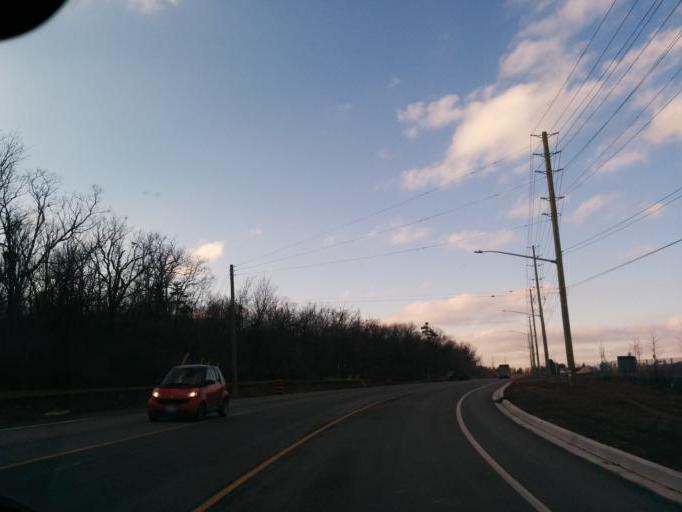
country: CA
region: Ontario
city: Oakville
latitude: 43.4888
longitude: -79.6776
